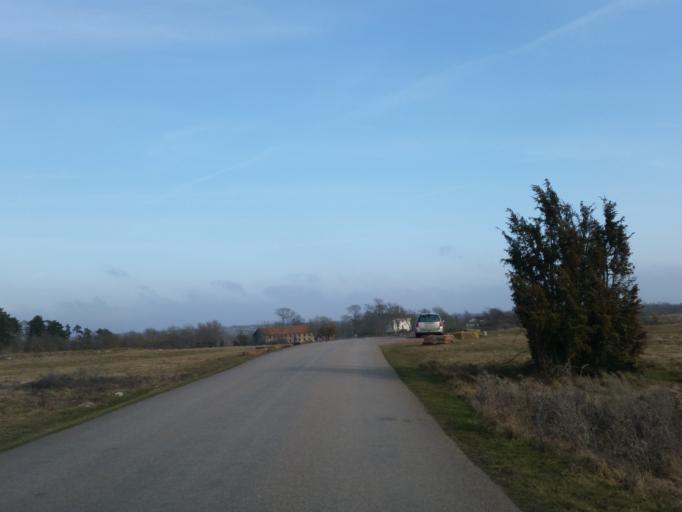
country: SE
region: Kalmar
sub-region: Borgholms Kommun
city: Borgholm
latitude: 56.8688
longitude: 16.6524
